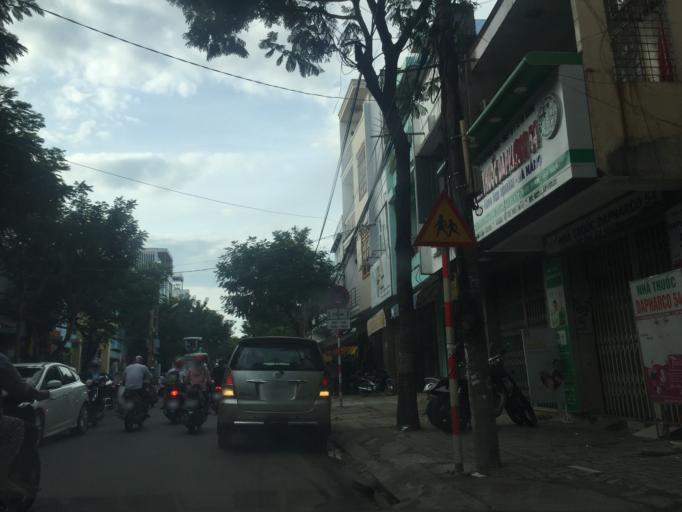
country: VN
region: Da Nang
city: Da Nang
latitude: 16.0757
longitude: 108.2124
